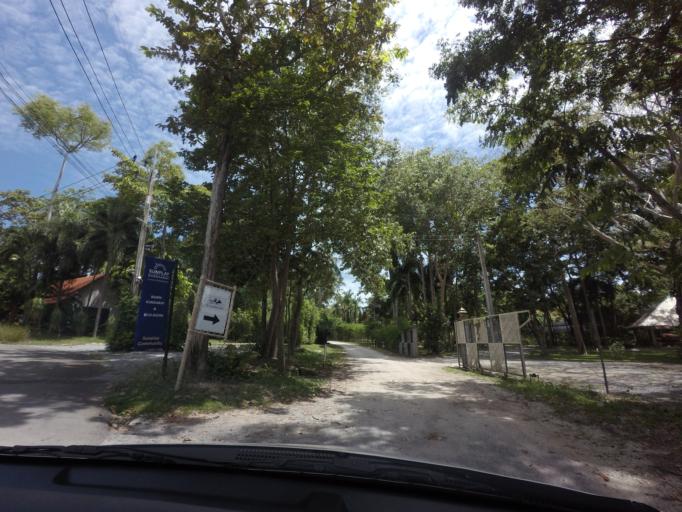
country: TH
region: Chon Buri
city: Sattahip
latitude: 12.7477
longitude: 100.9143
